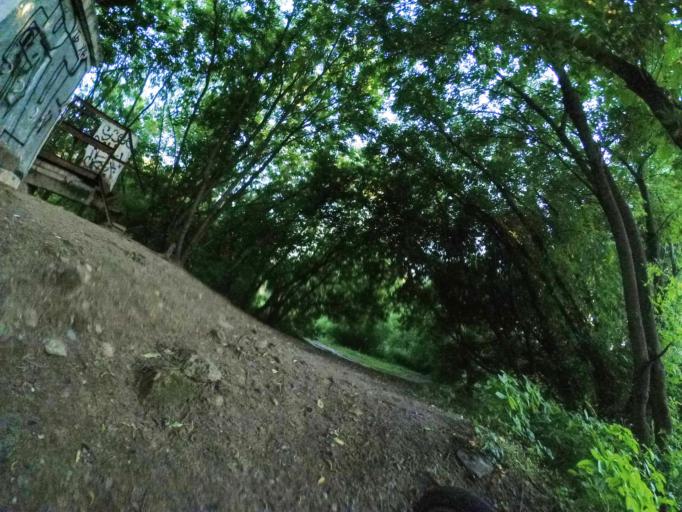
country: RU
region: Moscow
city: Strogino
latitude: 55.8303
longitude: 37.4258
